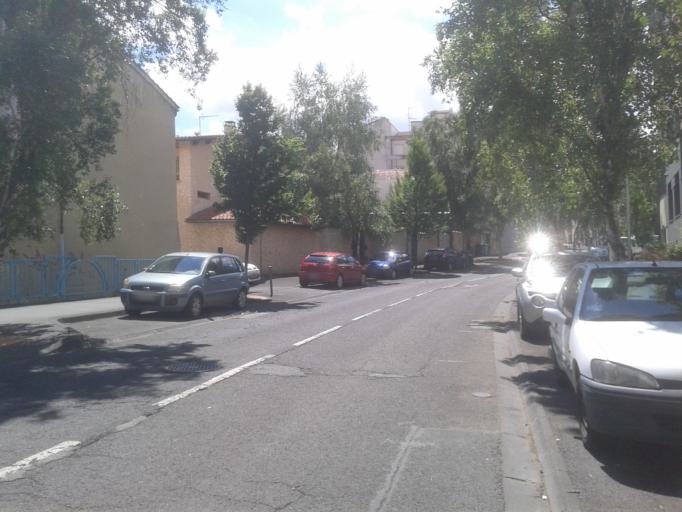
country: FR
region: Auvergne
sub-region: Departement du Puy-de-Dome
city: Clermont-Ferrand
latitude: 45.7844
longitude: 3.0801
